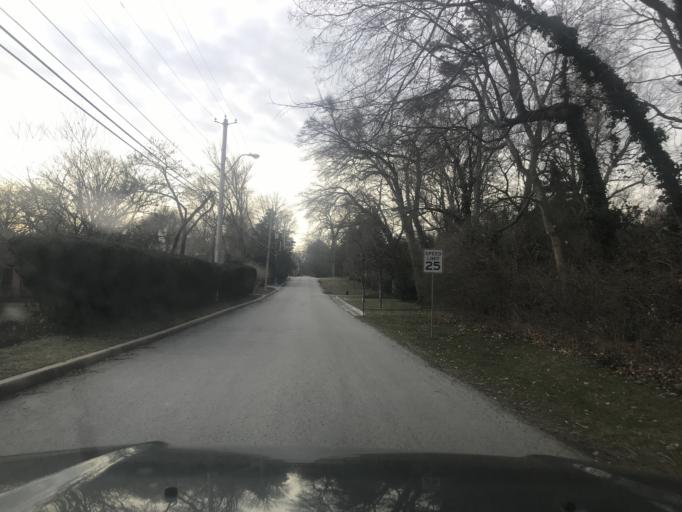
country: US
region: Kansas
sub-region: Johnson County
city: Westwood
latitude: 39.0308
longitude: -94.5994
